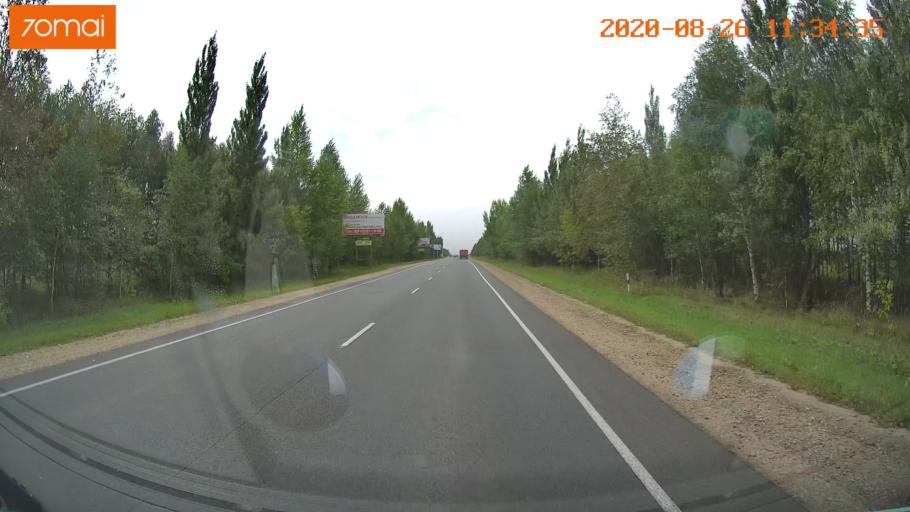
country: RU
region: Rjazan
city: Shilovo
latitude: 54.2839
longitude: 40.8421
